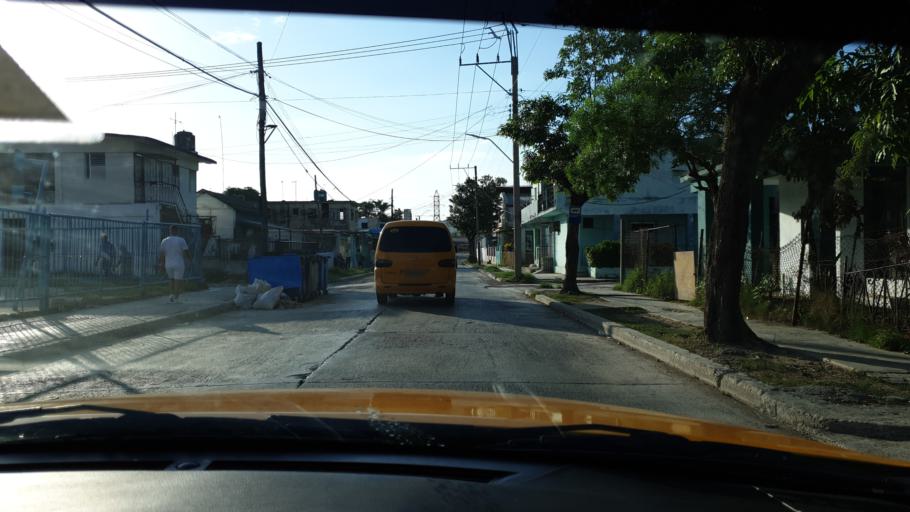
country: CU
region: La Habana
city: Regla
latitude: 23.1082
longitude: -82.3299
